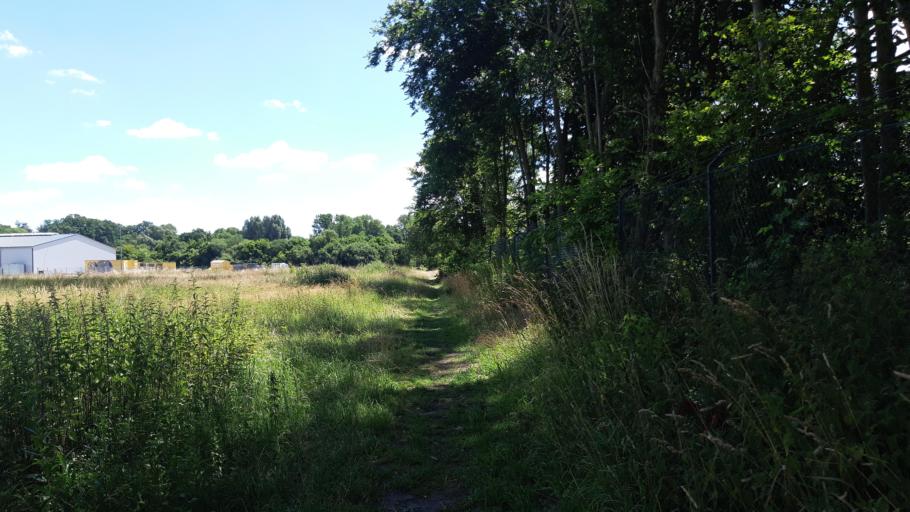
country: DE
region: Lower Saxony
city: Dahlem
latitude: 53.1905
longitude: 10.7465
